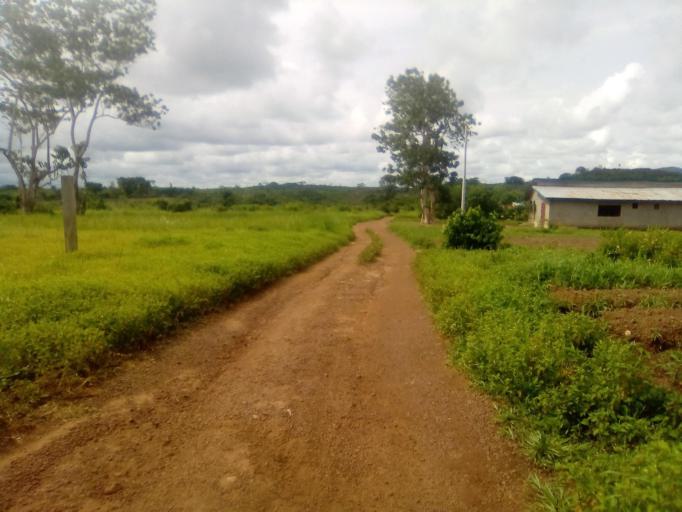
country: SL
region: Southern Province
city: Moyamba
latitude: 8.1475
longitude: -12.4317
